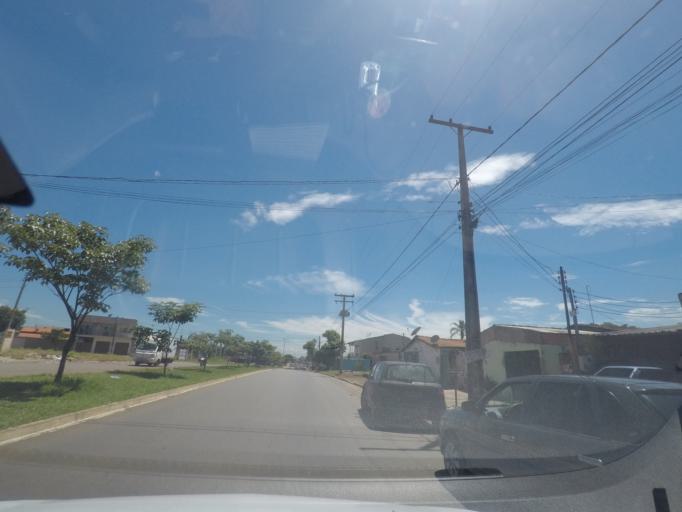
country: BR
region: Goias
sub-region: Aparecida De Goiania
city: Aparecida de Goiania
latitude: -16.7711
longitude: -49.3239
